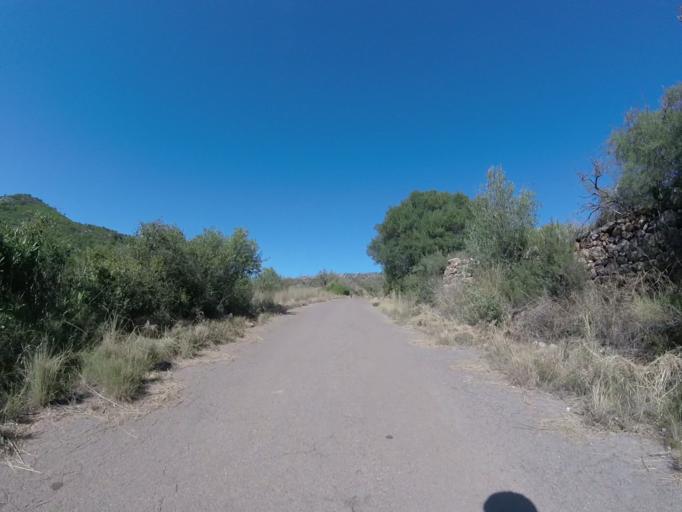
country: ES
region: Valencia
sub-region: Provincia de Castello
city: Orpesa/Oropesa del Mar
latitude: 40.1351
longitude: 0.1054
